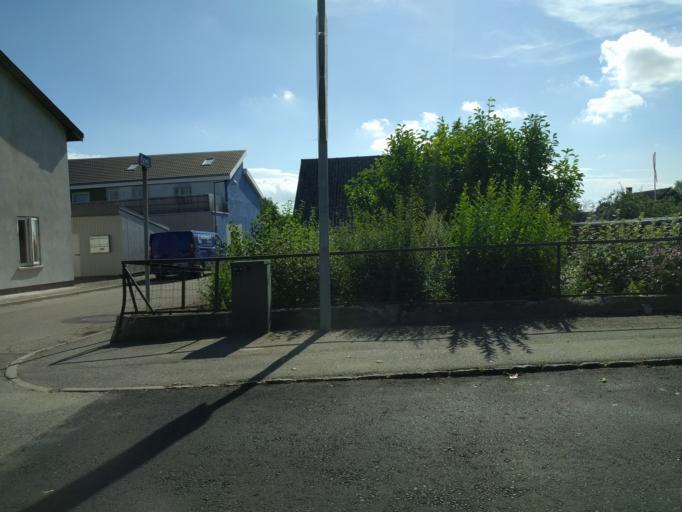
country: DK
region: Zealand
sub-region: Vordingborg Kommune
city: Stege
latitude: 54.9764
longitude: 12.2750
